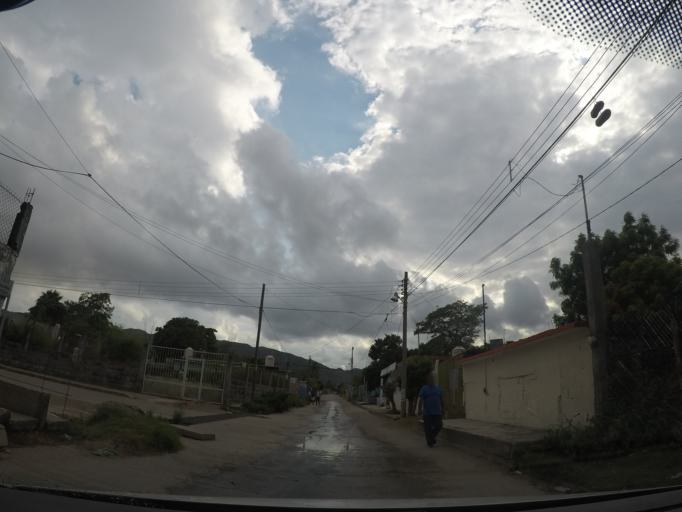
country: MX
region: Oaxaca
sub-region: Salina Cruz
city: Salina Cruz
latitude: 16.2123
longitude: -95.2076
